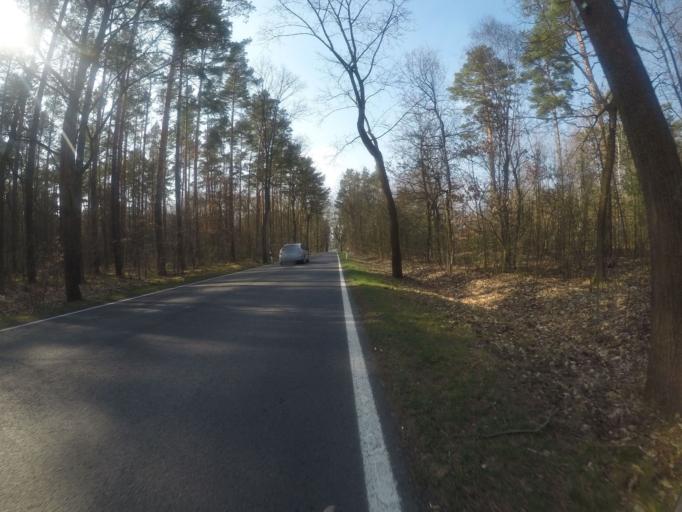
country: DE
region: Brandenburg
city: Bestensee
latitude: 52.2855
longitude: 13.7171
